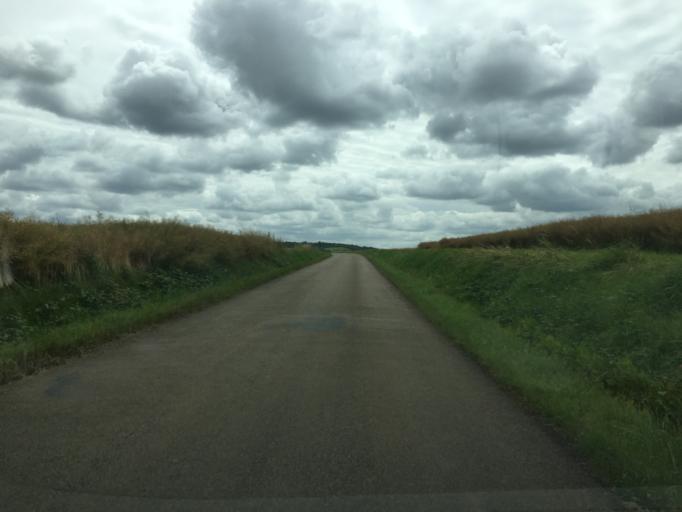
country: FR
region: Bourgogne
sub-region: Departement de l'Yonne
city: Fleury-la-Vallee
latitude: 47.8787
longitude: 3.4284
